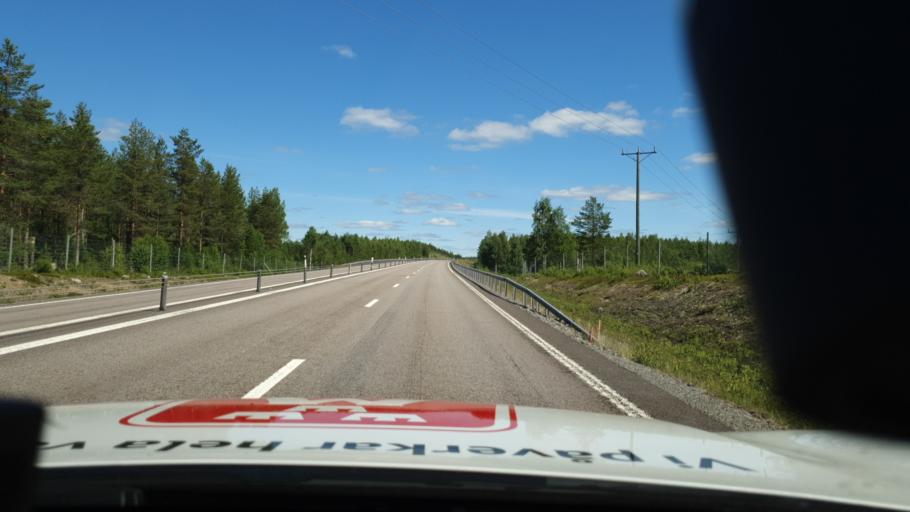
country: SE
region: Norrbotten
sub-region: Kalix Kommun
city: Toere
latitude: 65.9144
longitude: 22.7086
